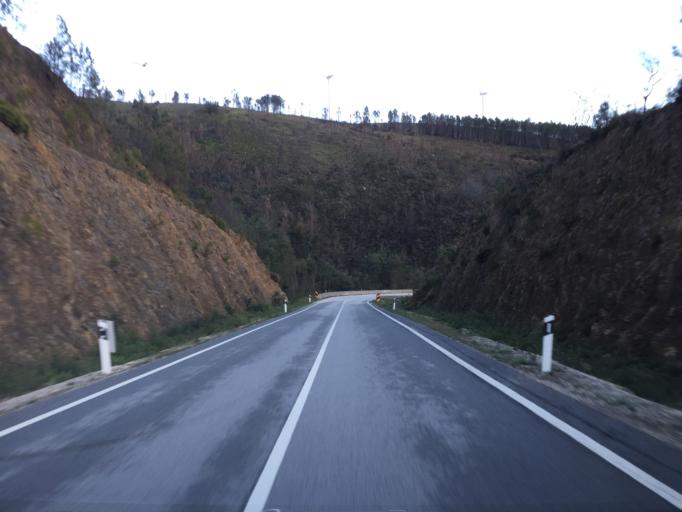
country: PT
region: Coimbra
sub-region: Pampilhosa da Serra
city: Pampilhosa da Serra
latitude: 40.1006
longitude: -7.9861
